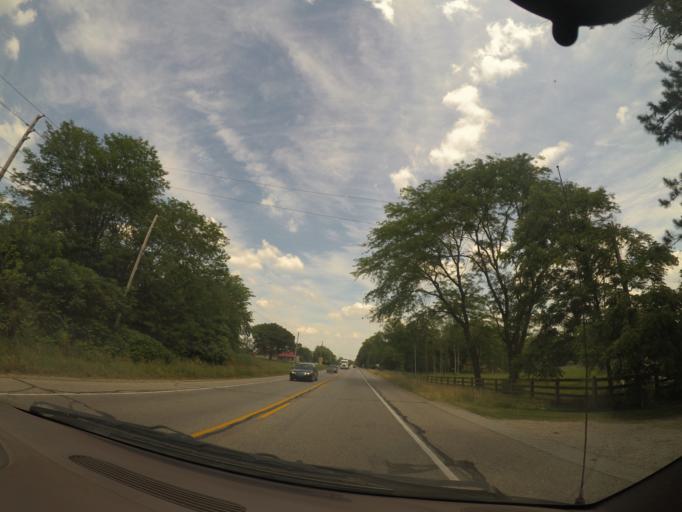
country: US
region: Indiana
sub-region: Elkhart County
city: Bristol
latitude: 41.6677
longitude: -85.7891
